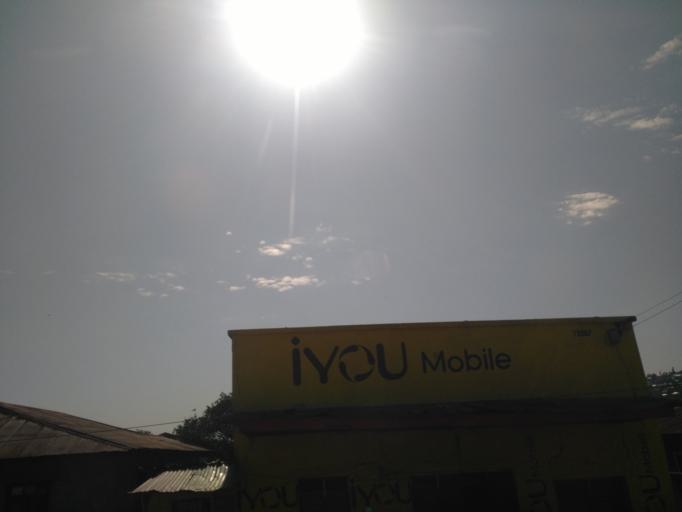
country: TZ
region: Mwanza
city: Mwanza
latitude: -2.4941
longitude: 32.8980
